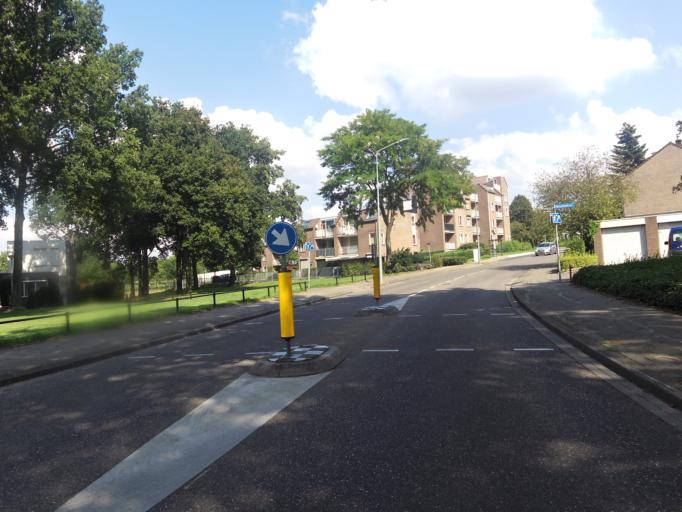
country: NL
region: Limburg
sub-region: Gemeente Brunssum
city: Brunssum
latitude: 50.9227
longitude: 5.9610
